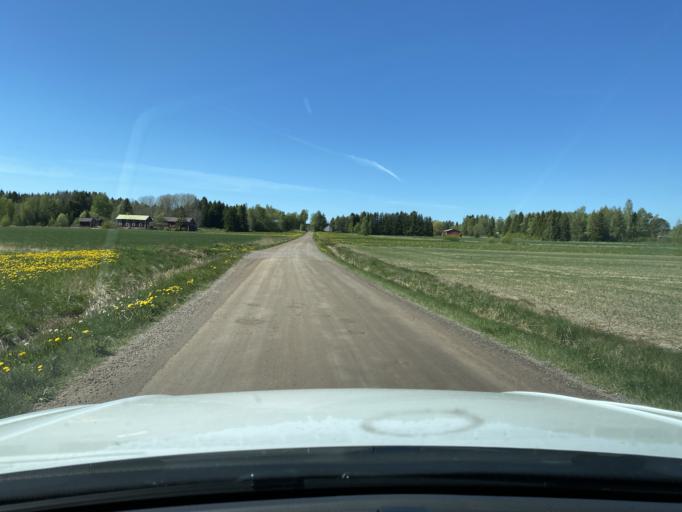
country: FI
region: Satakunta
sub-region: Rauma
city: Lappi
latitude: 61.1381
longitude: 21.9630
